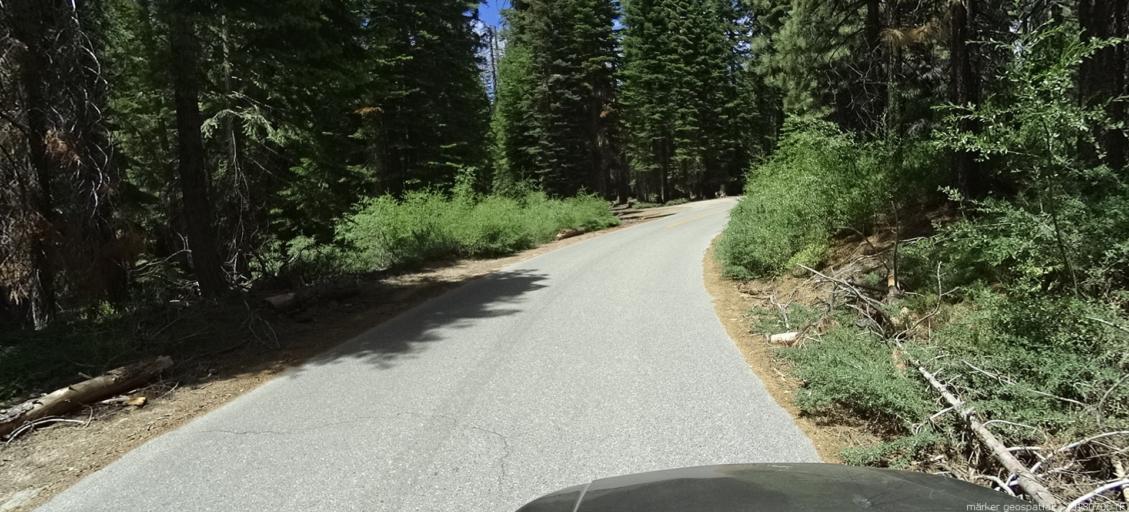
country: US
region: California
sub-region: Madera County
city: Oakhurst
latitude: 37.4407
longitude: -119.4395
